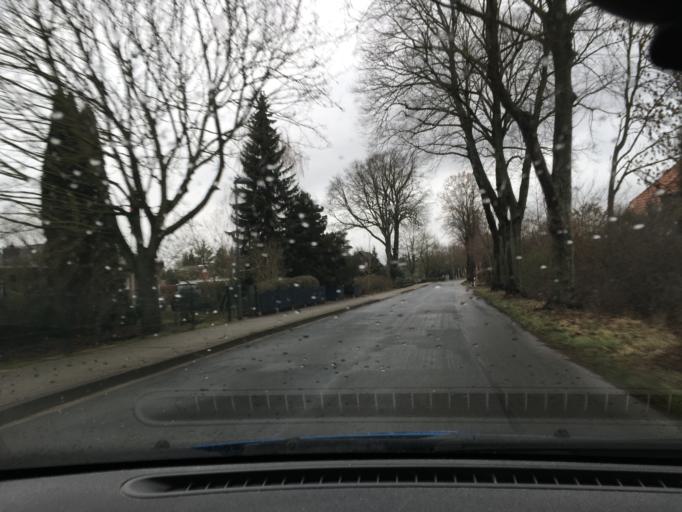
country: DE
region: Mecklenburg-Vorpommern
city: Nostorf
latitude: 53.3502
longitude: 10.6496
